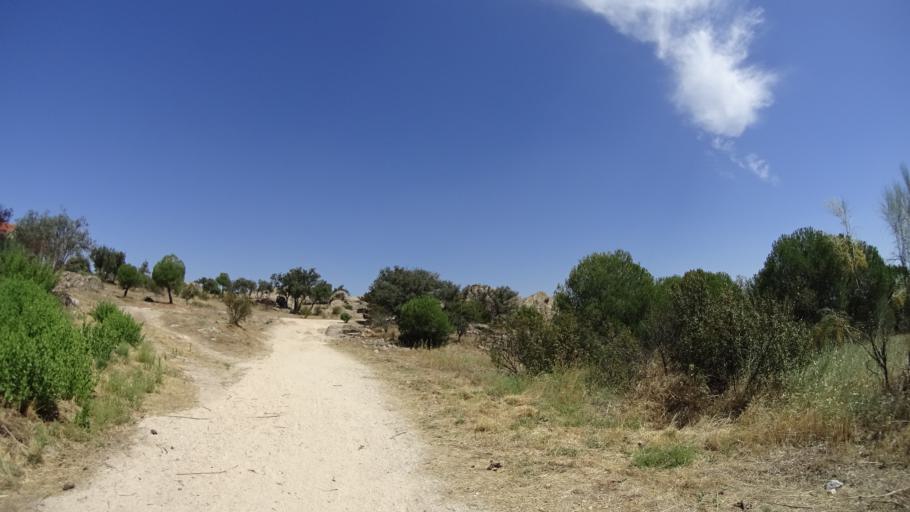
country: ES
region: Madrid
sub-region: Provincia de Madrid
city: Torrelodones
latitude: 40.5722
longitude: -3.9341
